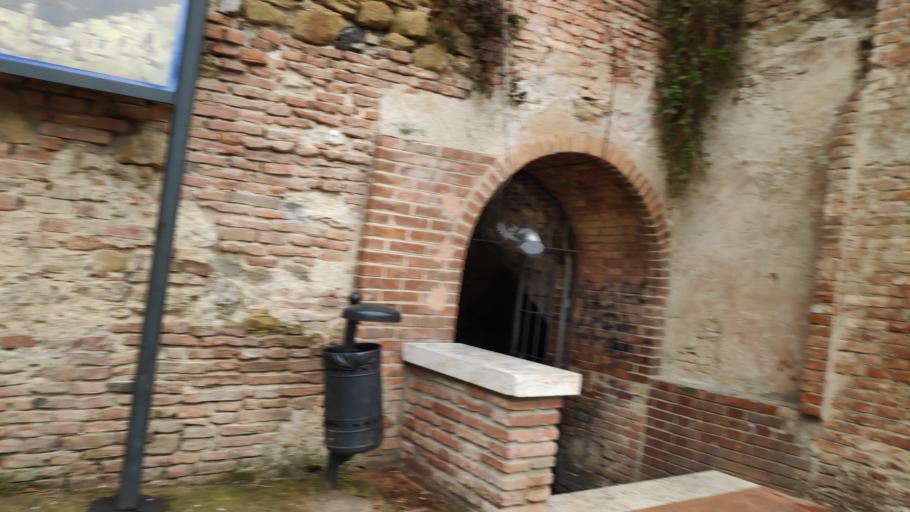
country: IT
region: Tuscany
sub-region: Provincia di Grosseto
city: Grosseto
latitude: 42.7586
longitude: 11.1142
